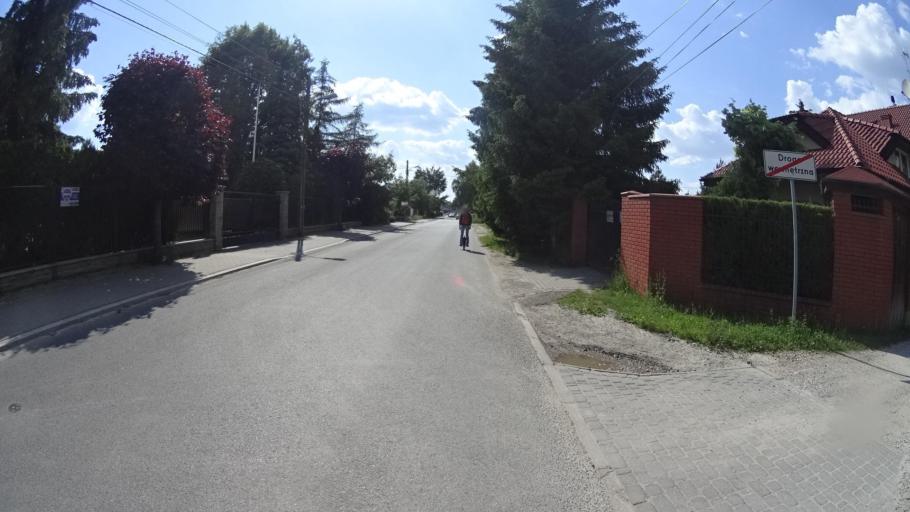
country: PL
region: Masovian Voivodeship
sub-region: Powiat piaseczynski
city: Mysiadlo
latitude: 52.1156
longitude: 21.0219
